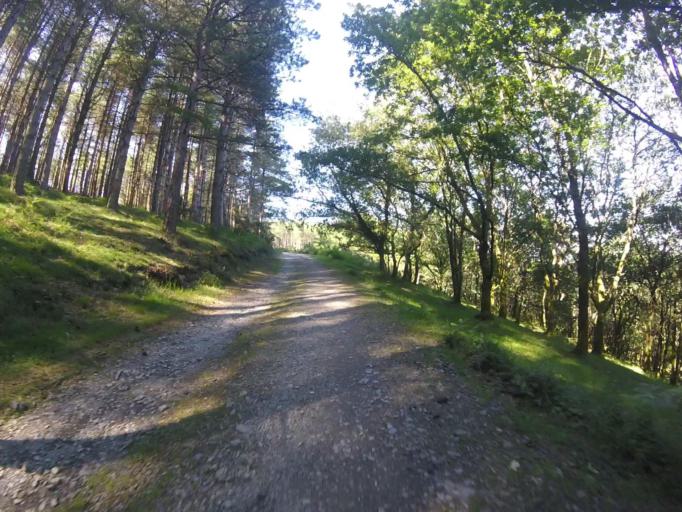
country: ES
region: Basque Country
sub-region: Provincia de Guipuzcoa
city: Irun
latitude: 43.2962
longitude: -1.7856
